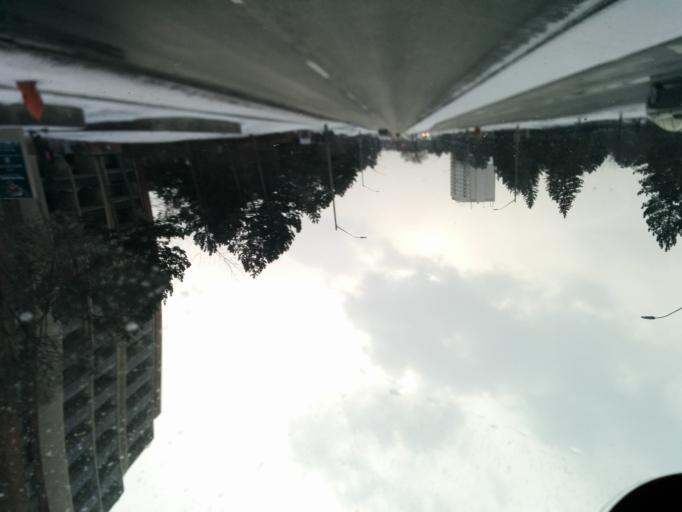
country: CA
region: Ontario
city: Mississauga
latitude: 43.5827
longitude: -79.7540
